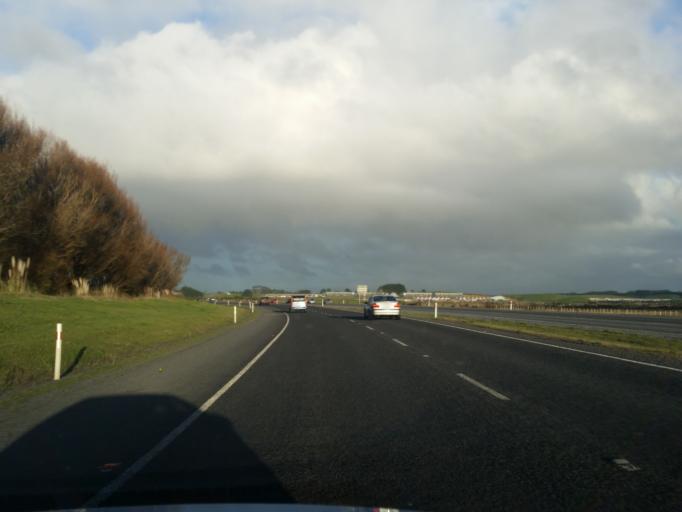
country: NZ
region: Waikato
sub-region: Waikato District
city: Te Kauwhata
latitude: -37.3442
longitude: 175.0684
